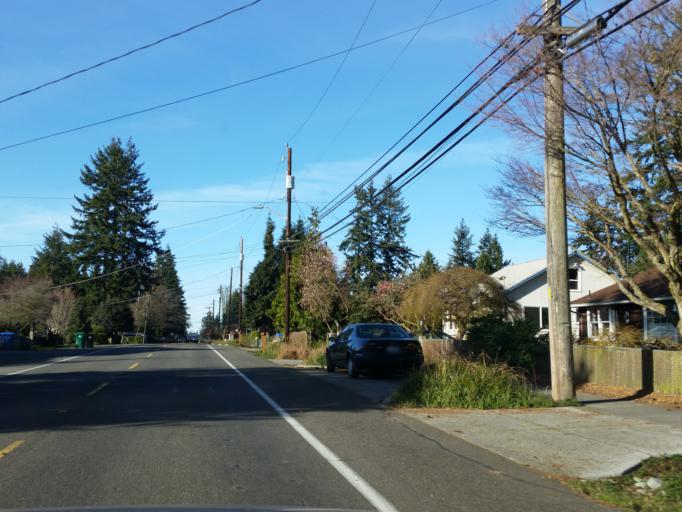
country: US
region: Washington
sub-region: King County
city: Shoreline
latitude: 47.7658
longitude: -122.3404
